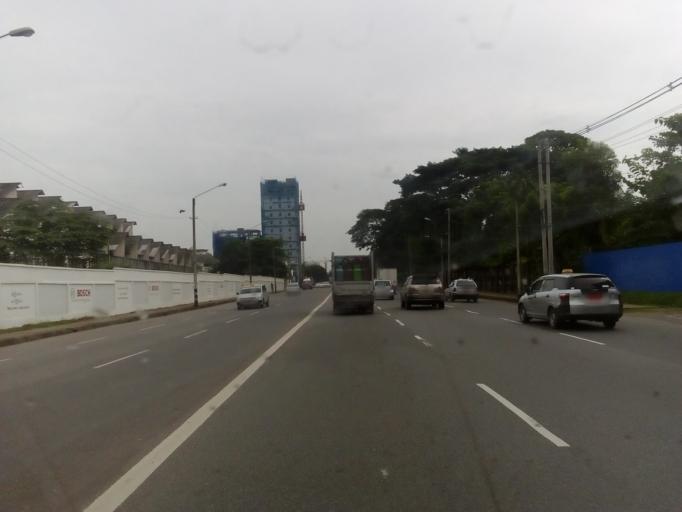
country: MM
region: Yangon
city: Yangon
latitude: 16.8440
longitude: 96.1567
